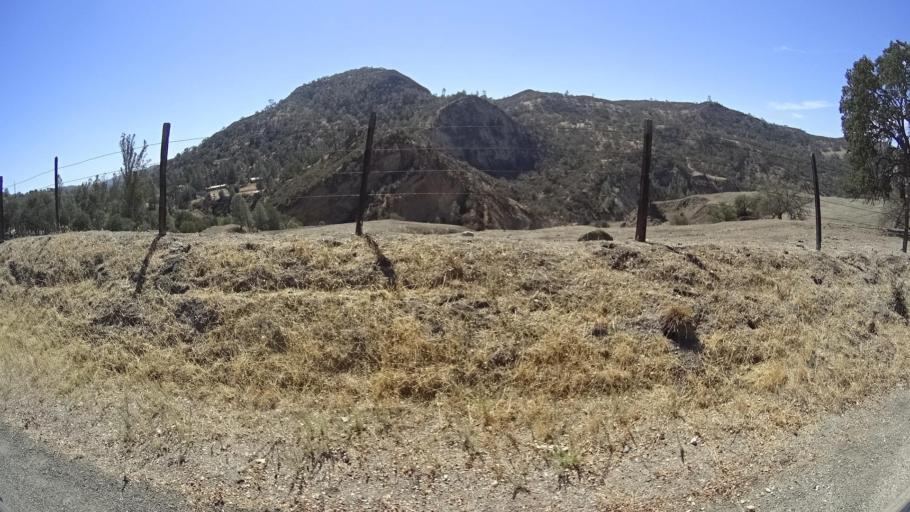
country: US
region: California
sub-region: Fresno County
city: Coalinga
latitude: 36.0928
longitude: -120.6732
